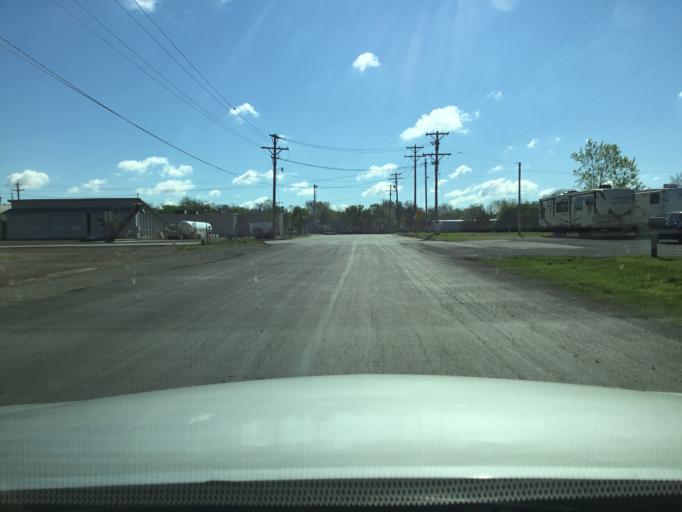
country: US
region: Kansas
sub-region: Allen County
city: Iola
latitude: 37.9284
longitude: -95.4120
